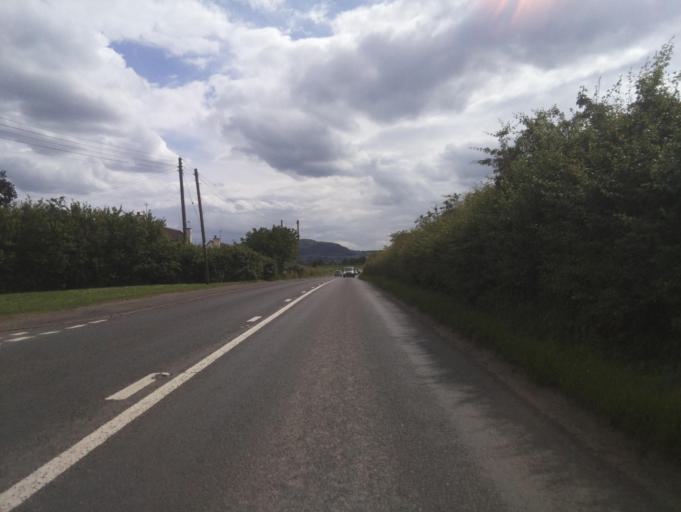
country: GB
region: England
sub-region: Worcestershire
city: Bransford
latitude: 52.1622
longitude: -2.3098
